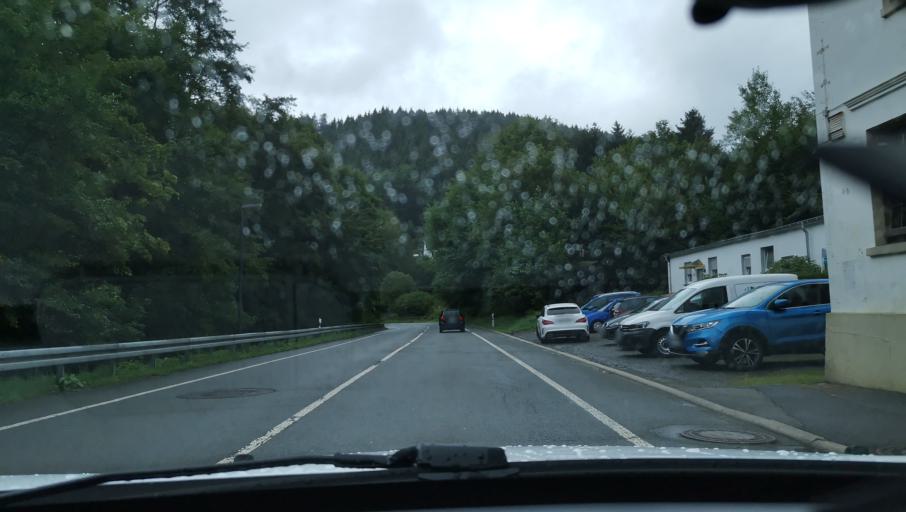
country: DE
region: North Rhine-Westphalia
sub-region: Regierungsbezirk Arnsberg
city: Schalksmuhle
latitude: 51.2190
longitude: 7.5362
